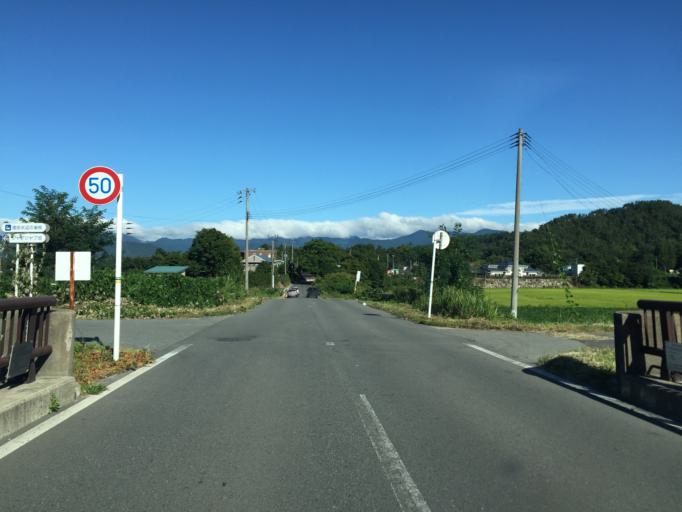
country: JP
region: Yamagata
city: Yonezawa
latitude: 37.9538
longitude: 140.1346
